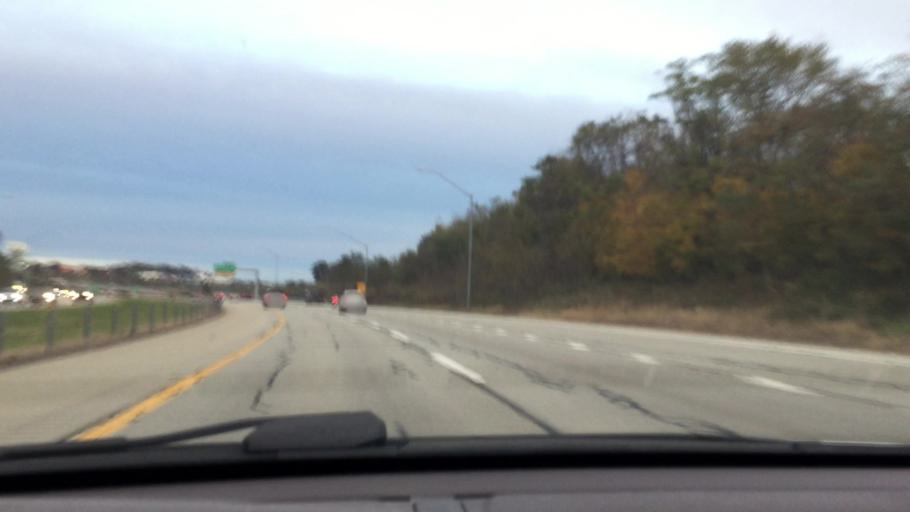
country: US
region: Pennsylvania
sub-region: Allegheny County
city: Cheswick
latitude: 40.5610
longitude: -79.8006
